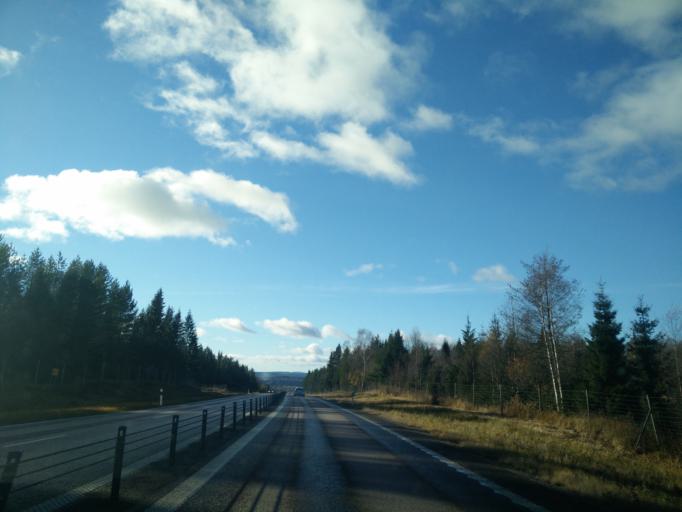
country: SE
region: Vaesternorrland
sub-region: Timra Kommun
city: Soraker
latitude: 62.5334
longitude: 17.5068
